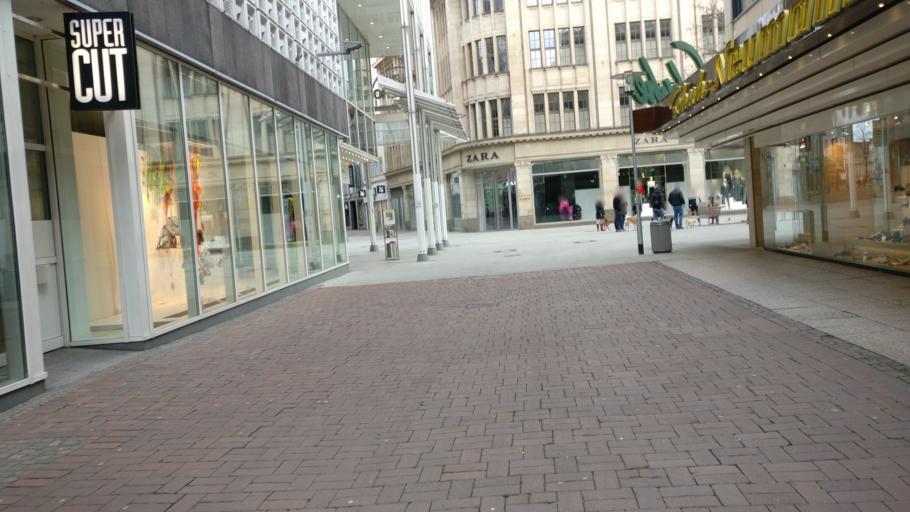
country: DE
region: Lower Saxony
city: Hannover
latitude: 52.3728
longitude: 9.7363
